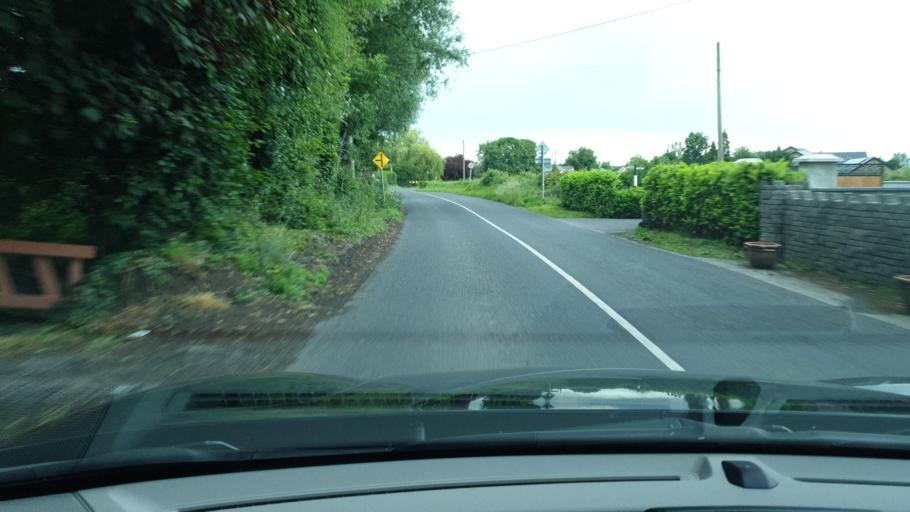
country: IE
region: Leinster
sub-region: An Mhi
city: Navan
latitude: 53.6325
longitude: -6.7110
